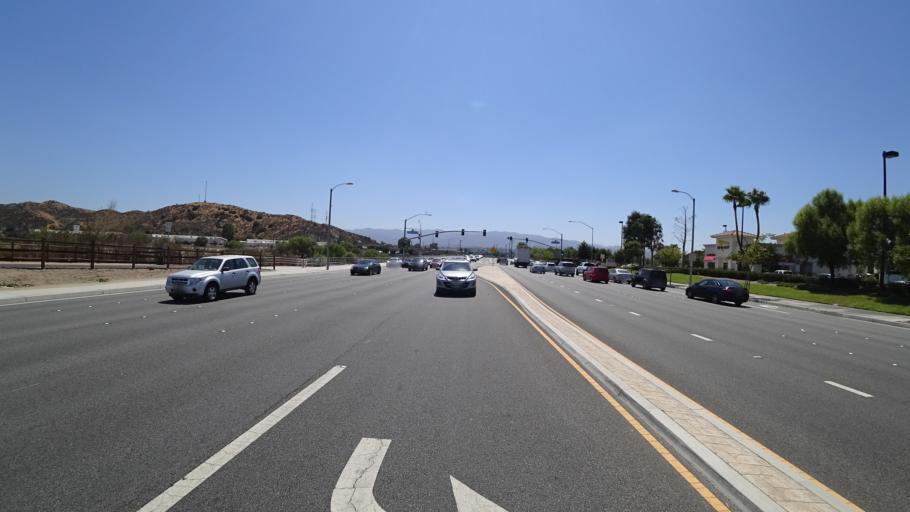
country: US
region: California
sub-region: Los Angeles County
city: Santa Clarita
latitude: 34.4255
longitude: -118.5385
